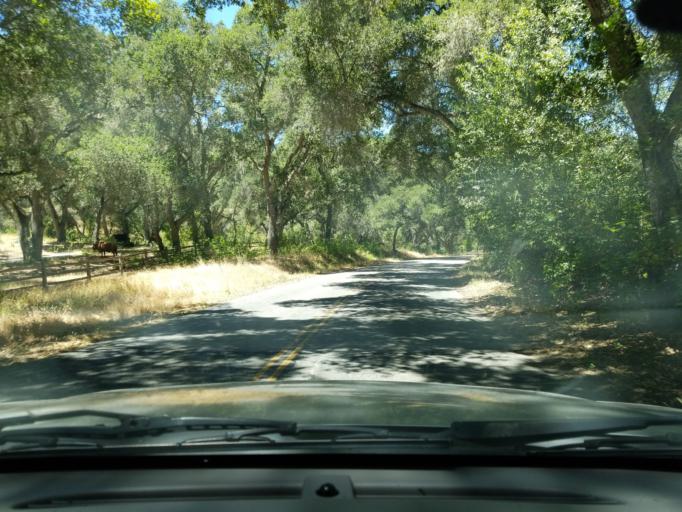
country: US
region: California
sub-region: Monterey County
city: Chualar
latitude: 36.4151
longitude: -121.6025
